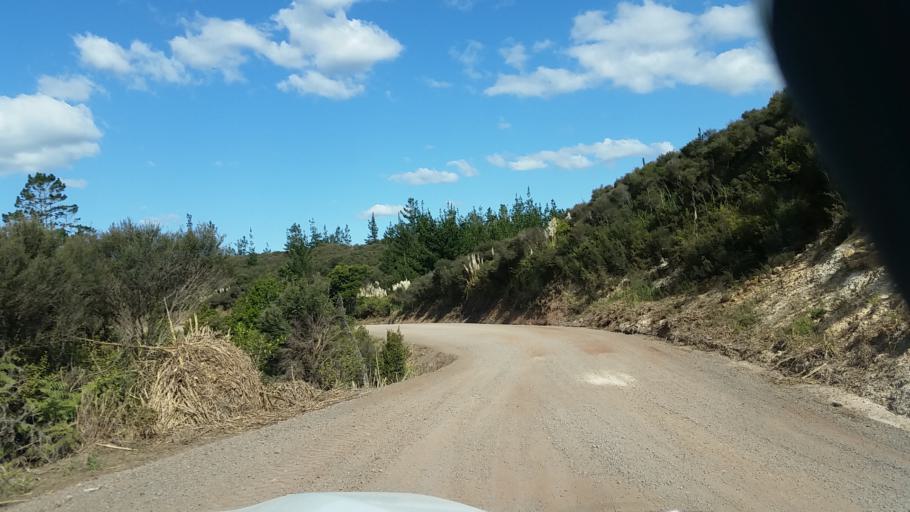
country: NZ
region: Northland
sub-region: Whangarei
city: Whangarei
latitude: -35.5912
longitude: 174.3160
